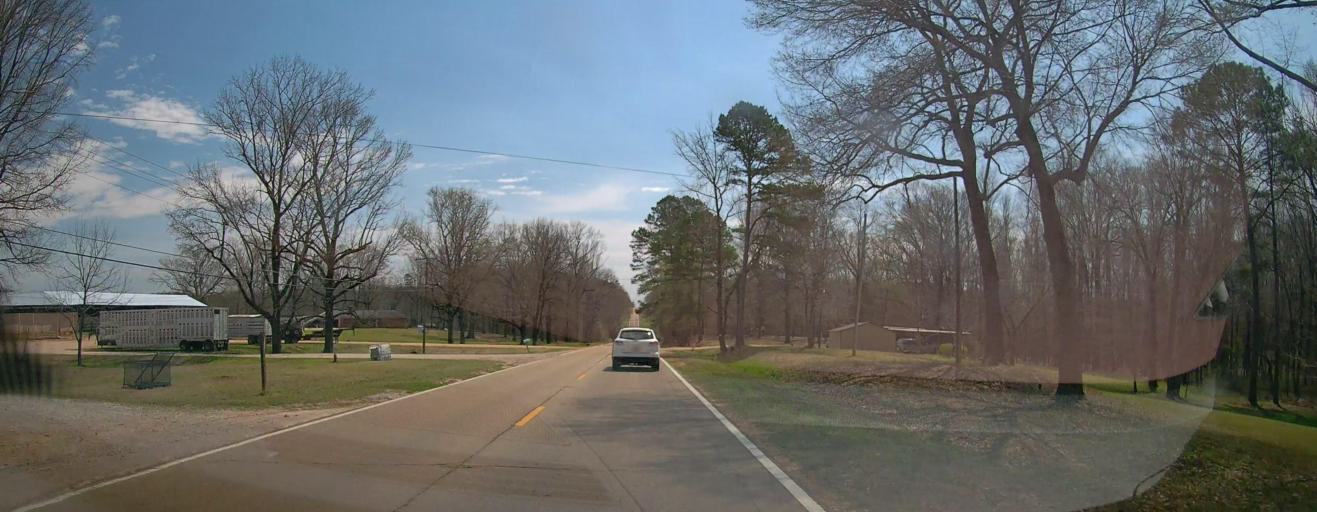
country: US
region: Mississippi
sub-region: Union County
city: New Albany
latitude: 34.4460
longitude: -88.9665
